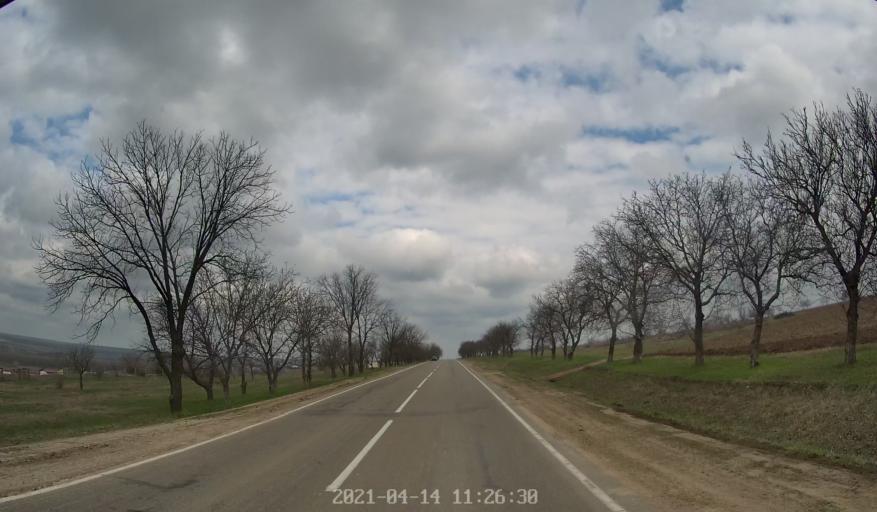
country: MD
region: Criuleni
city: Criuleni
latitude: 47.1645
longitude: 29.1634
